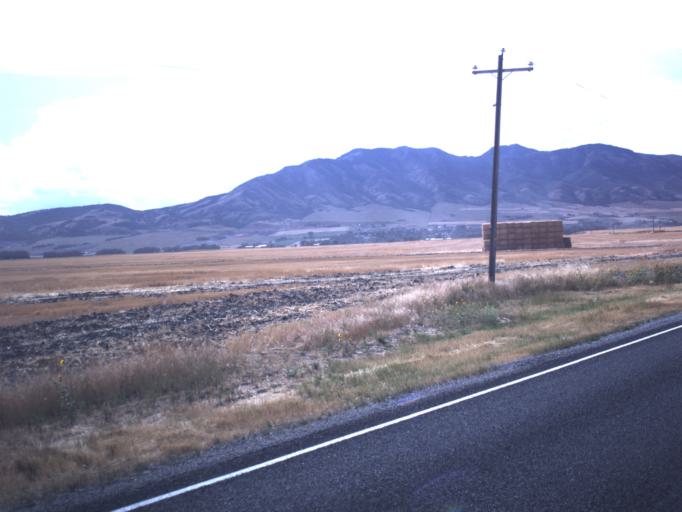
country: US
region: Utah
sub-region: Cache County
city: Benson
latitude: 41.9182
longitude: -112.0034
